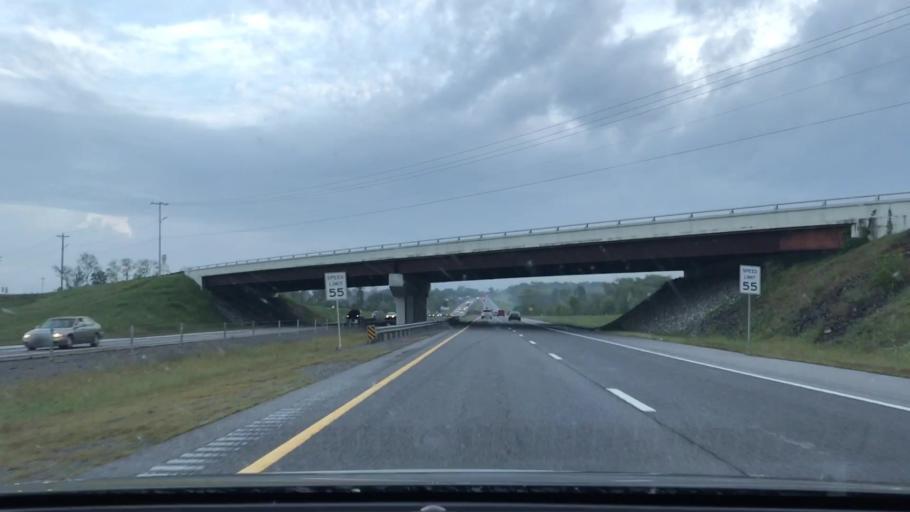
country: US
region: Tennessee
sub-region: Sumner County
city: Gallatin
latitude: 36.3775
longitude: -86.5028
